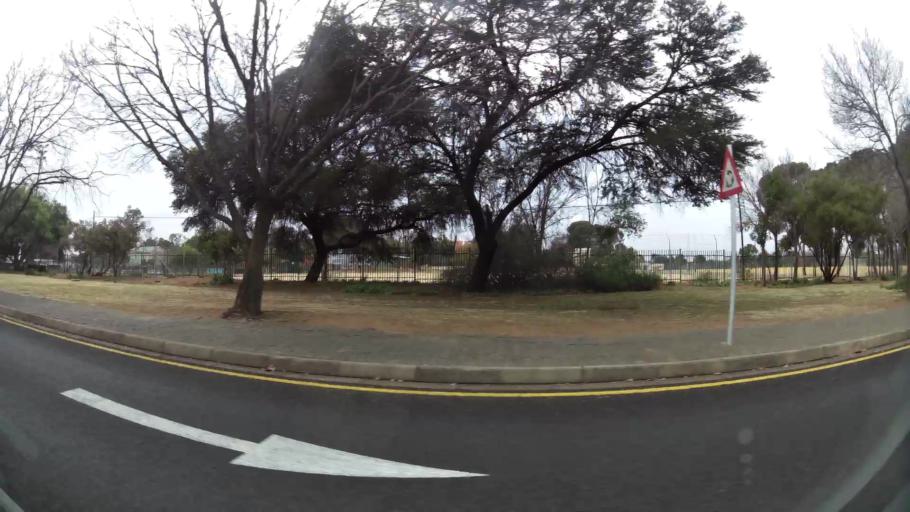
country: ZA
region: Orange Free State
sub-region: Mangaung Metropolitan Municipality
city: Bloemfontein
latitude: -29.1107
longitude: 26.1918
